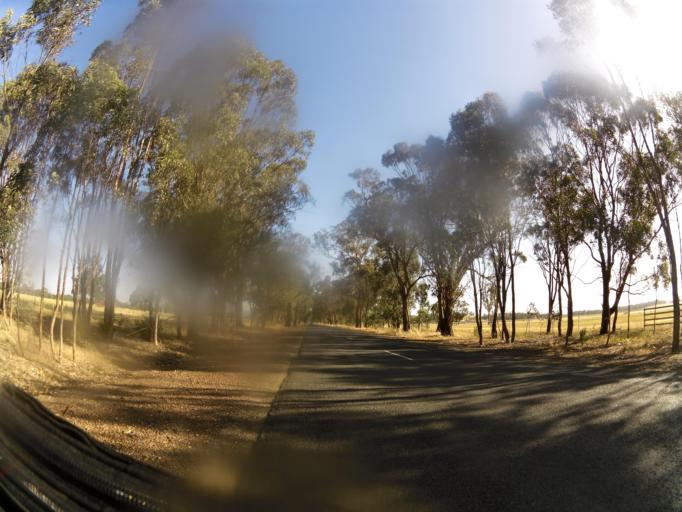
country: AU
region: Victoria
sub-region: Murrindindi
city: Kinglake West
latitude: -36.9768
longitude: 145.1102
